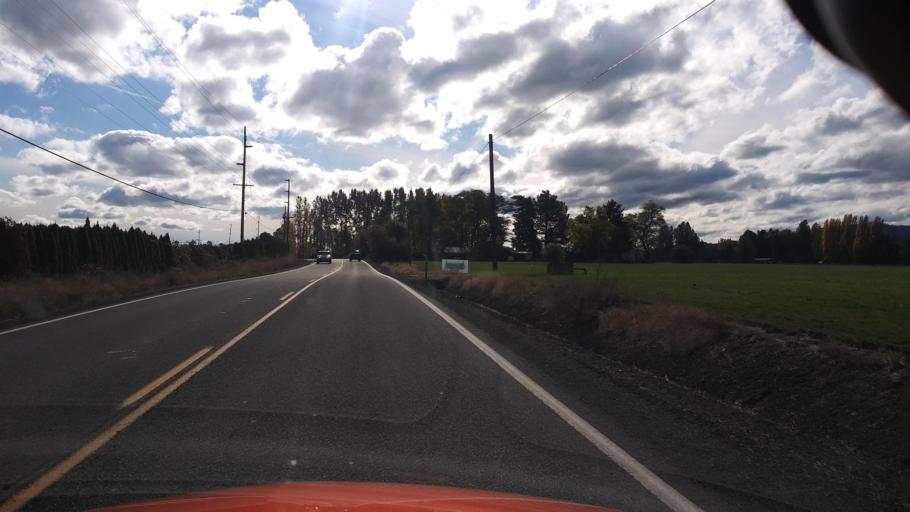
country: US
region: Oregon
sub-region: Washington County
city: Banks
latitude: 45.5851
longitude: -123.1144
